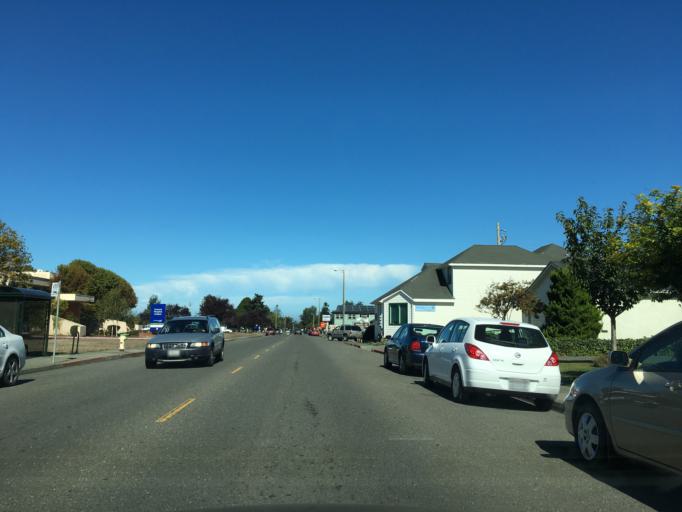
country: US
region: California
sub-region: Humboldt County
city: Myrtletown
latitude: 40.7876
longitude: -124.1396
